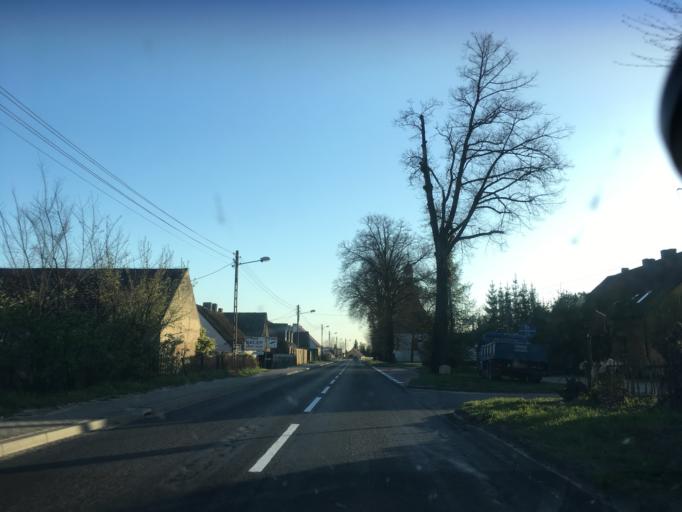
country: PL
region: Lubusz
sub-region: Powiat gorzowski
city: Jenin
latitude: 52.7068
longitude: 15.1366
